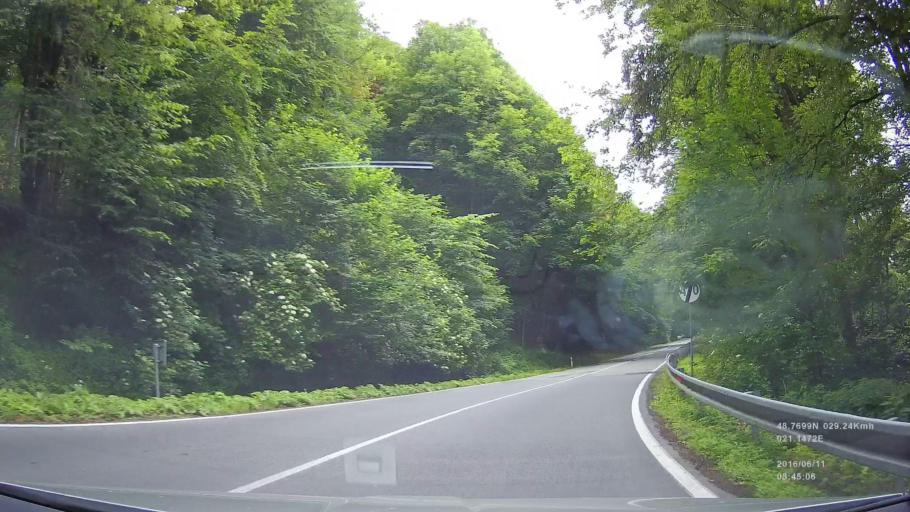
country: SK
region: Kosicky
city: Kosice
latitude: 48.7557
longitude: 21.1954
